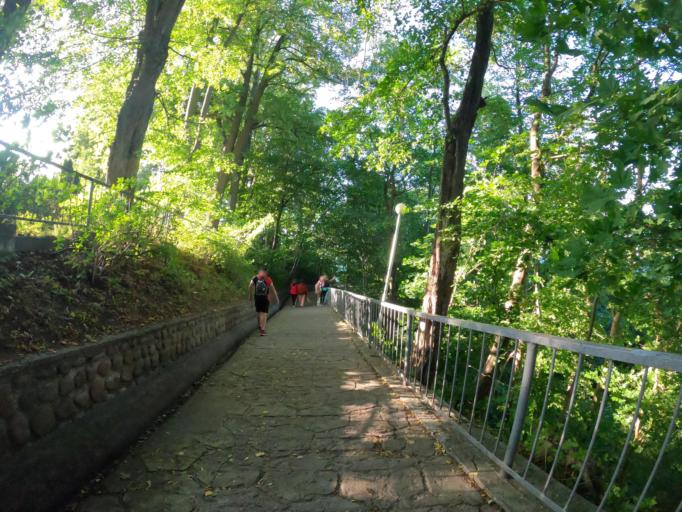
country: RU
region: Kaliningrad
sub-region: Gorod Svetlogorsk
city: Svetlogorsk
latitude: 54.9450
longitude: 20.1520
